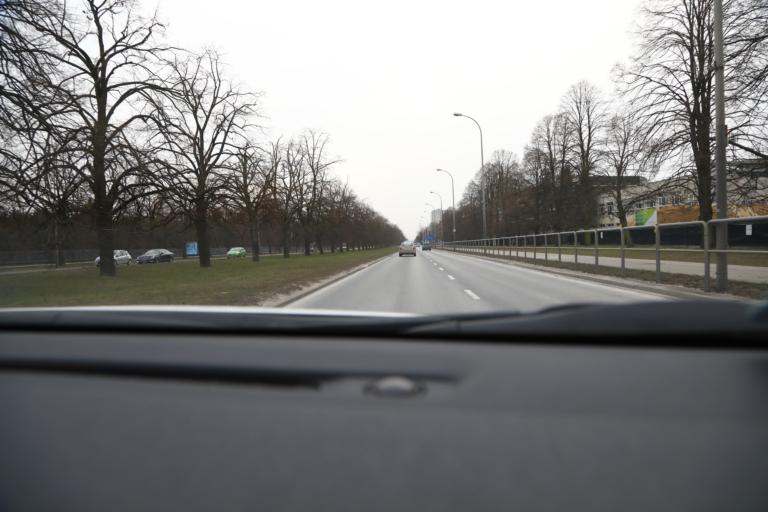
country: PL
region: Masovian Voivodeship
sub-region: Warszawa
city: Ochota
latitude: 52.2081
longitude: 20.9870
